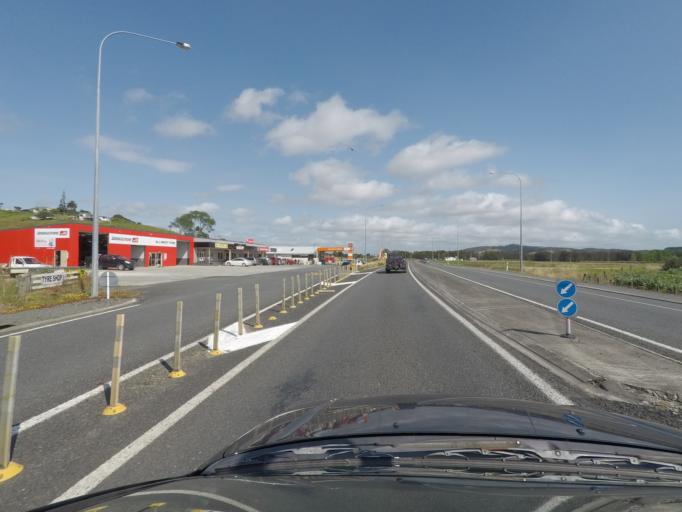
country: NZ
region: Northland
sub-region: Whangarei
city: Ruakaka
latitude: -35.8929
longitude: 174.4347
